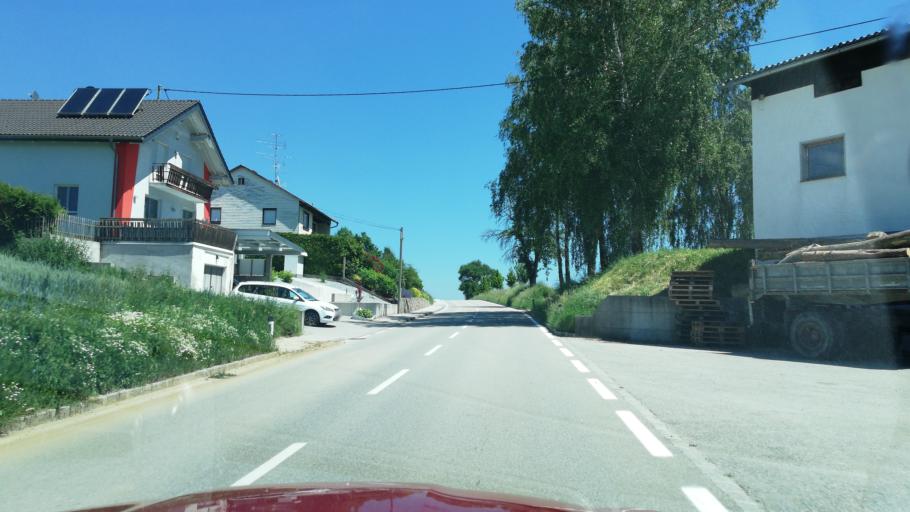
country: AT
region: Upper Austria
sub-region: Wels-Land
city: Bachmanning
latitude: 48.1276
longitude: 13.7798
